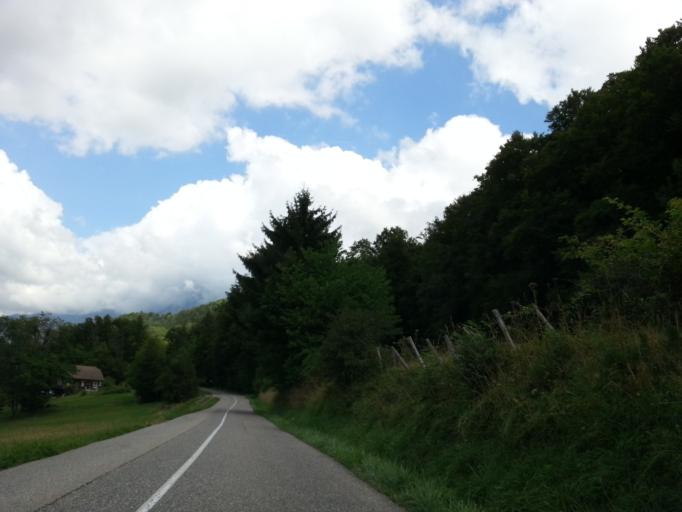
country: FR
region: Rhone-Alpes
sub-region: Departement de la Haute-Savoie
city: Menthon-Saint-Bernard
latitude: 45.8627
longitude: 6.2172
